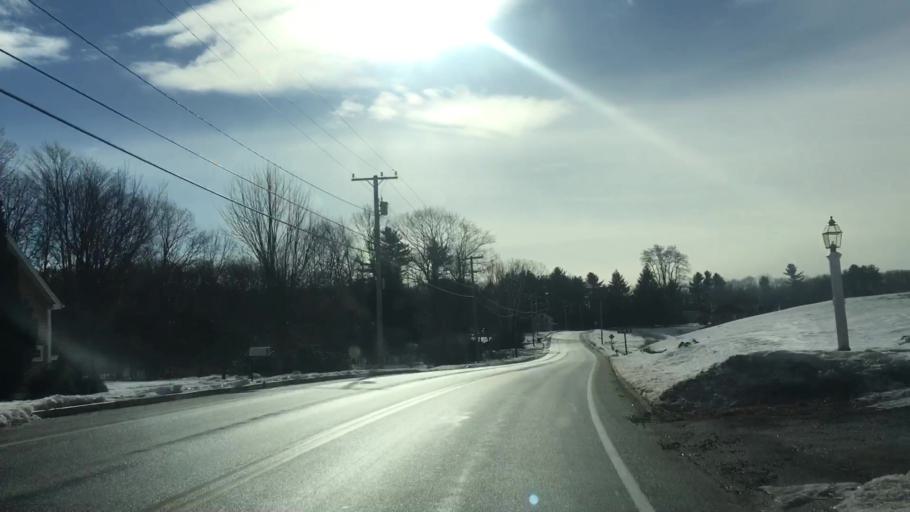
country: US
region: Maine
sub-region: York County
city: West Kennebunk
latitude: 43.4180
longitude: -70.5642
